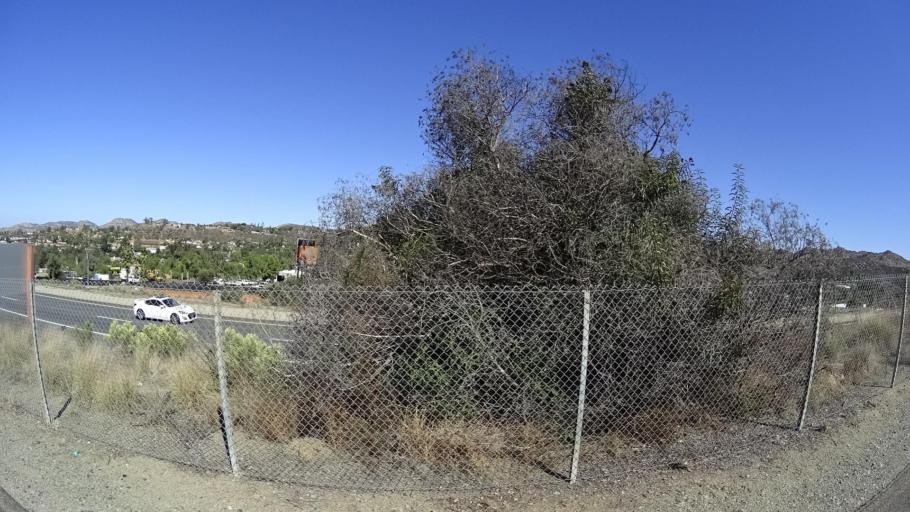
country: US
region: California
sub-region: San Diego County
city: Harbison Canyon
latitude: 32.8562
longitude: -116.8299
